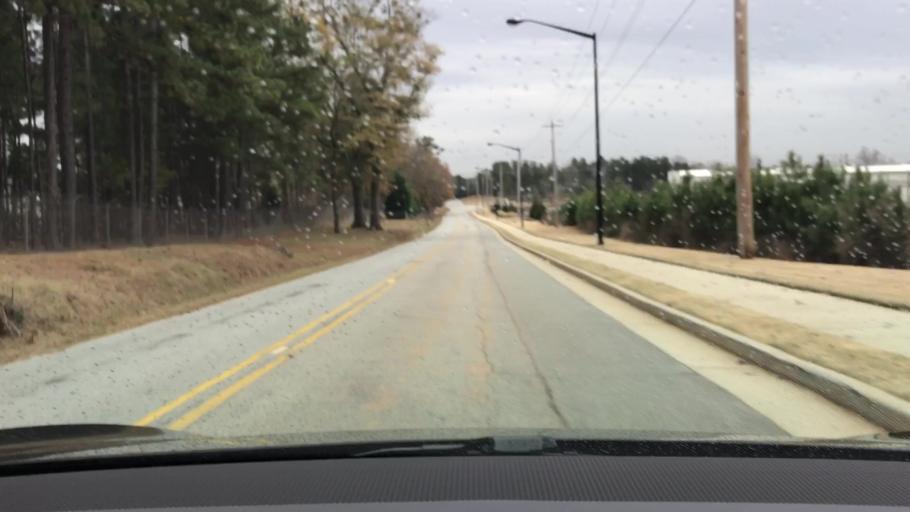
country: US
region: Georgia
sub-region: Gwinnett County
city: Buford
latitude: 34.1112
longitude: -84.0100
